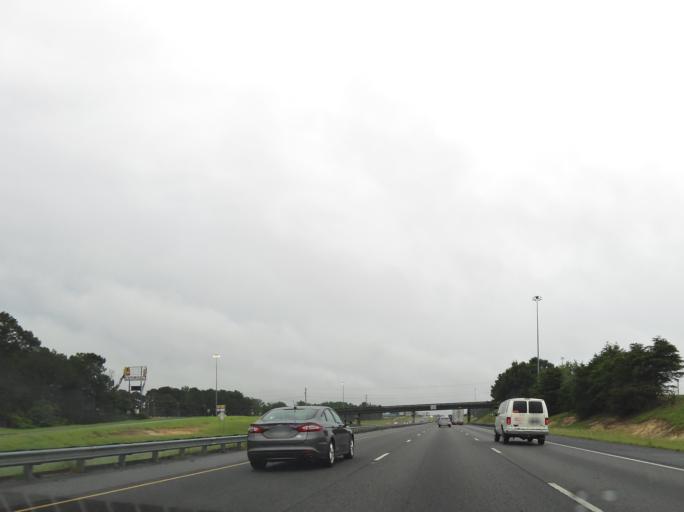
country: US
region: Georgia
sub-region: Crisp County
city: Cordele
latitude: 31.9088
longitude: -83.7385
